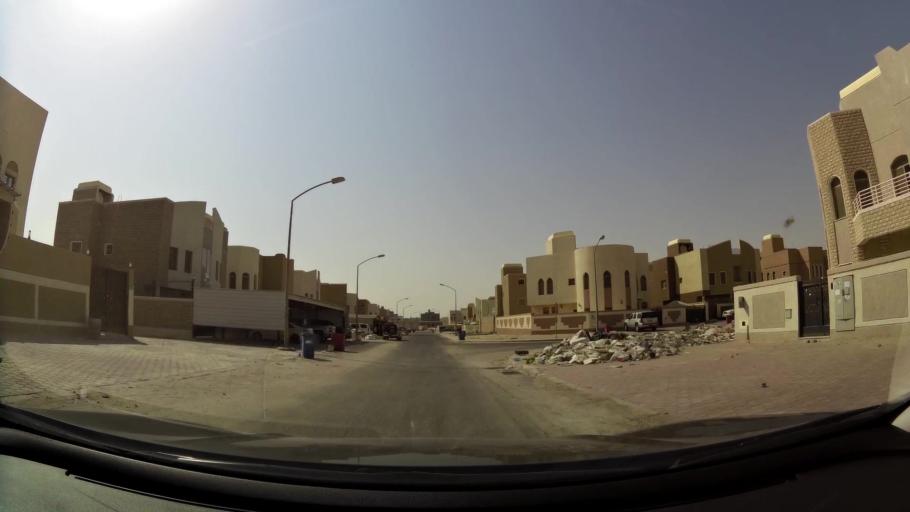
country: KW
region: Al Ahmadi
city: Al Wafrah
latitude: 28.8013
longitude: 48.0584
